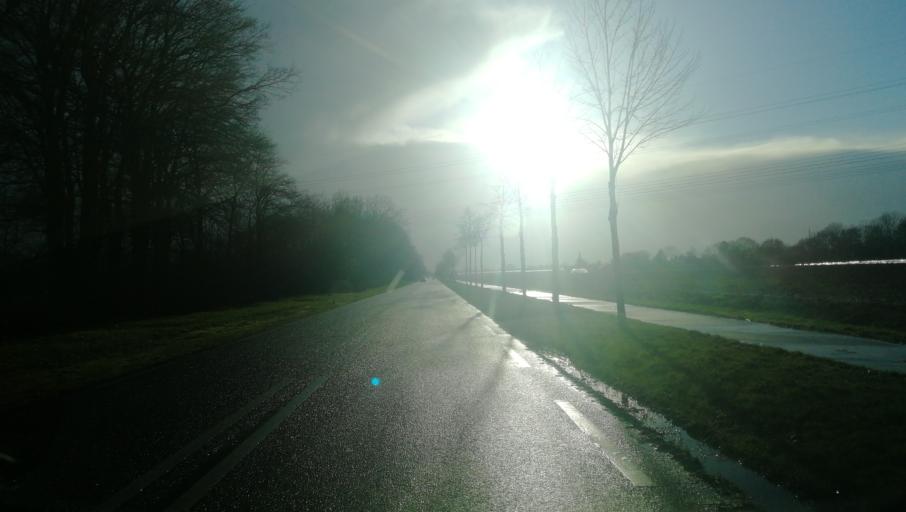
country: NL
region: Limburg
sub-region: Gemeente Peel en Maas
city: Maasbree
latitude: 51.3621
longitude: 6.0754
